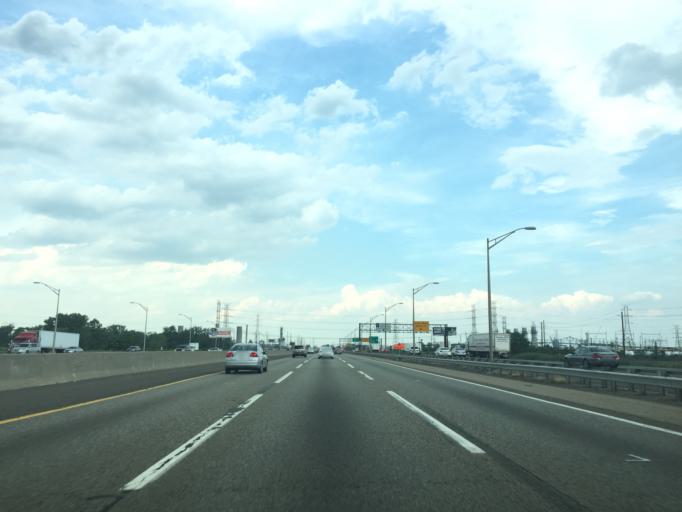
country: US
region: New Jersey
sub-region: Union County
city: Linden
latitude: 40.6190
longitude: -74.2195
